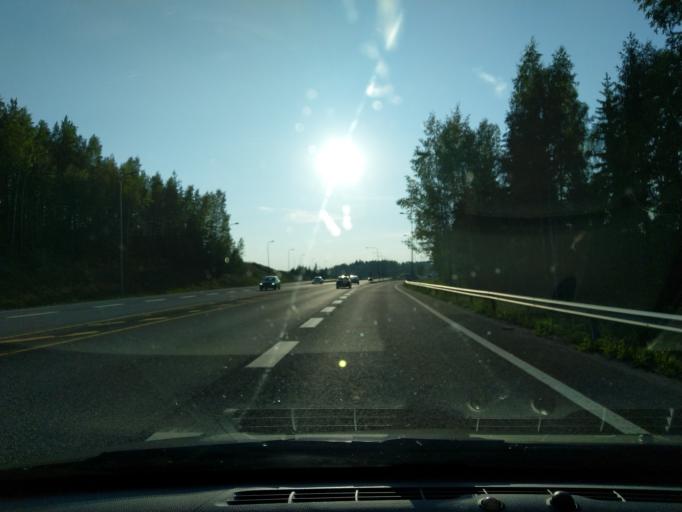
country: FI
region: Paijanne Tavastia
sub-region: Lahti
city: Lahti
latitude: 60.9679
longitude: 25.7322
